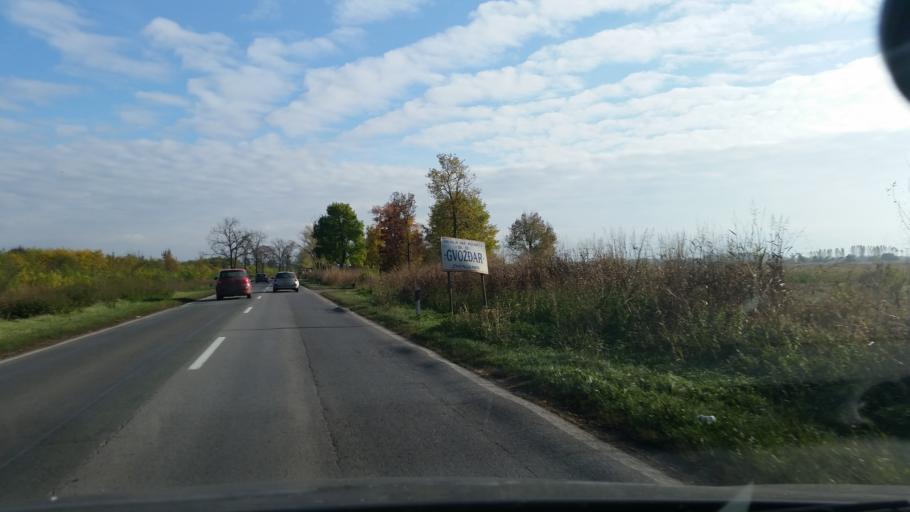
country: RS
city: Ecka
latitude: 45.3422
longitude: 20.4299
